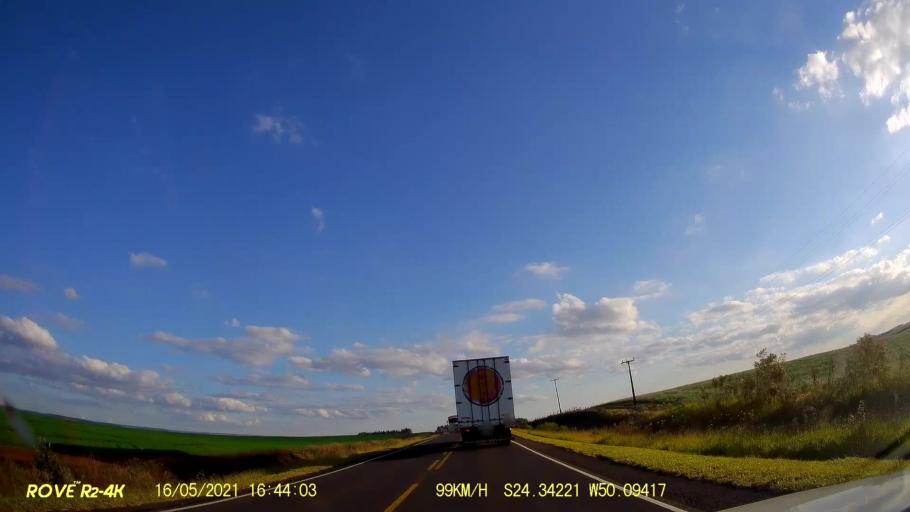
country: BR
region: Parana
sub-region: Pirai Do Sul
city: Pirai do Sul
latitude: -24.3425
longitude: -50.0943
